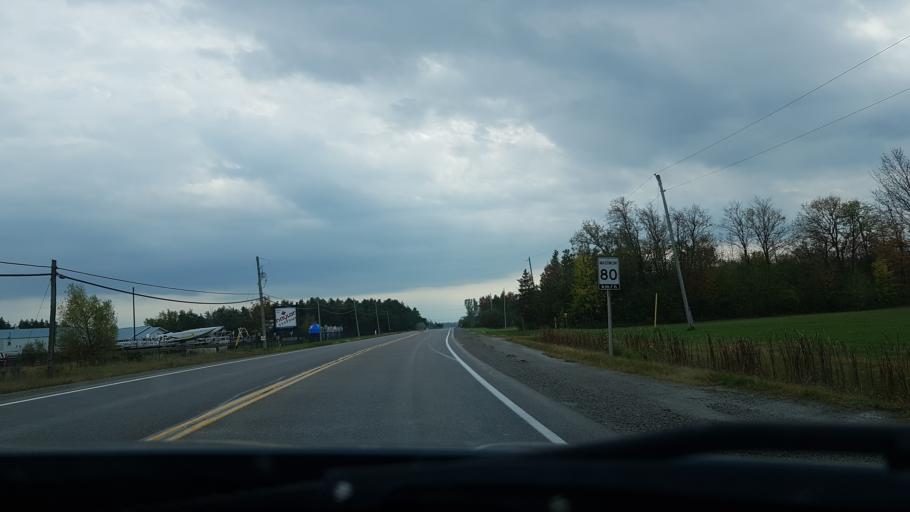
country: CA
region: Ontario
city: Omemee
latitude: 44.4315
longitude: -78.7778
